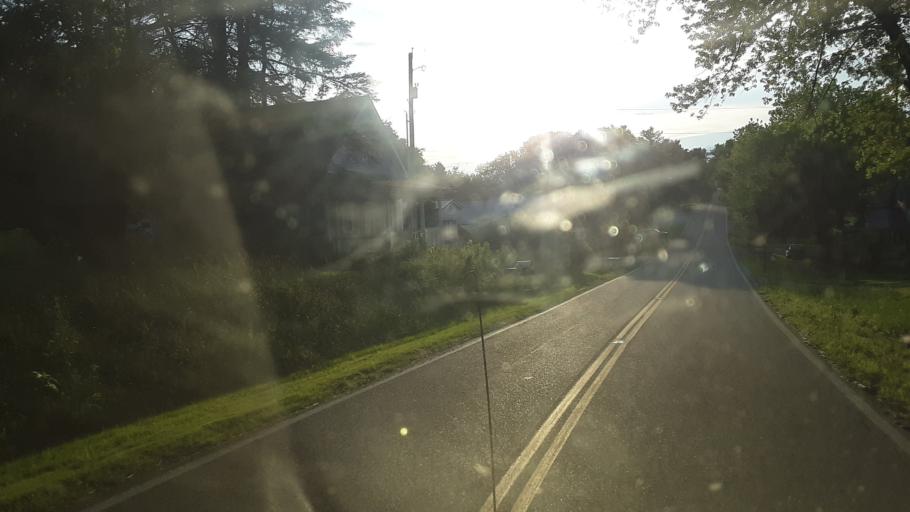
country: US
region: Ohio
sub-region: Harrison County
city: Cadiz
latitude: 40.3997
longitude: -81.0272
